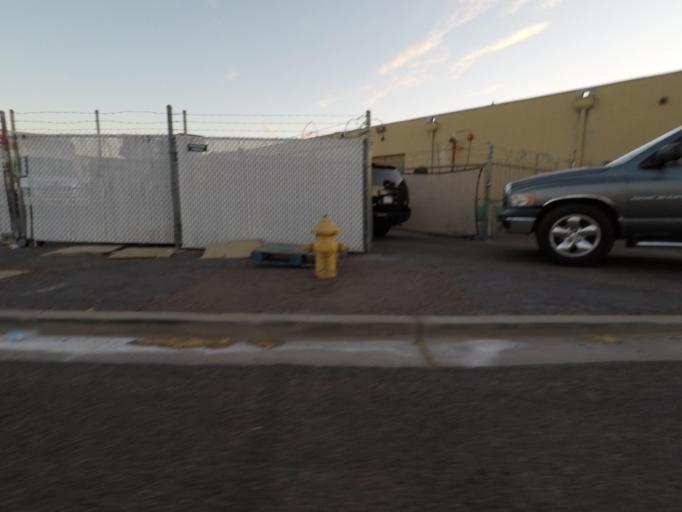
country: US
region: Arizona
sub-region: Maricopa County
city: Glendale
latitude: 33.4918
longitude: -112.1327
